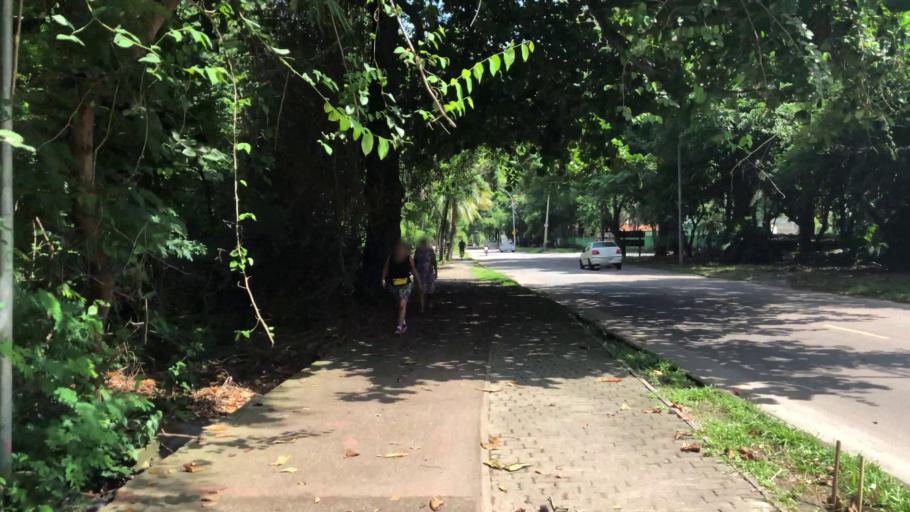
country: BR
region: Rio de Janeiro
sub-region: Rio De Janeiro
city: Rio de Janeiro
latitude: -23.0077
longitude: -43.3221
